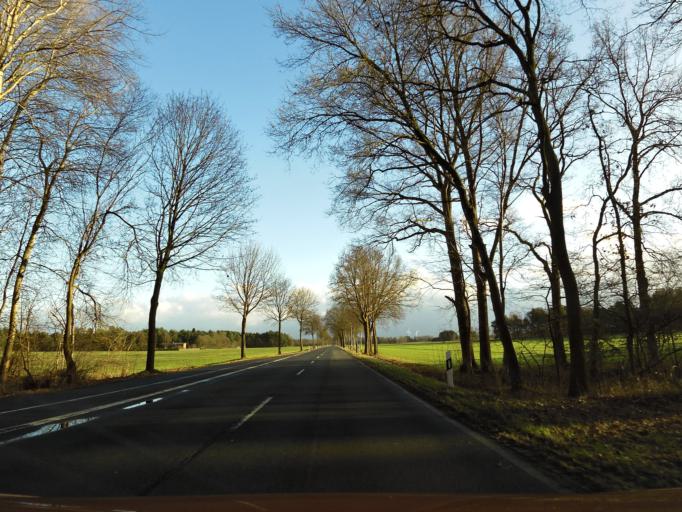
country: DE
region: Lower Saxony
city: Essel
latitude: 52.6859
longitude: 9.7348
